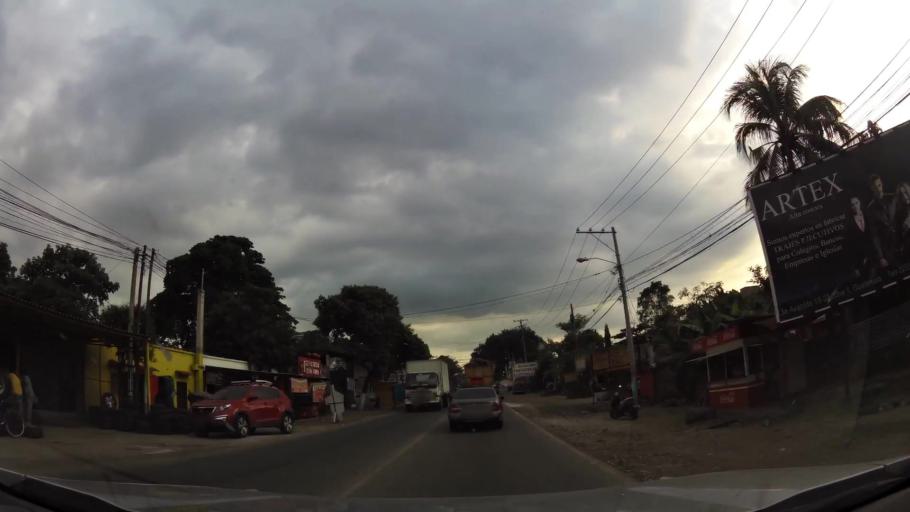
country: GT
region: Escuintla
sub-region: Municipio de Escuintla
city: Escuintla
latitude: 14.2965
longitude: -90.7825
